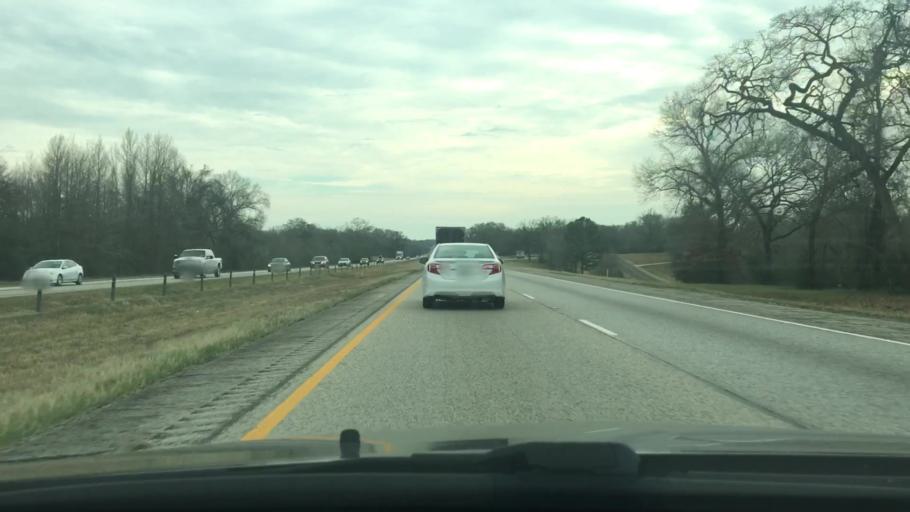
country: US
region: Texas
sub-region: Leon County
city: Centerville
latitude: 31.1994
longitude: -95.9945
